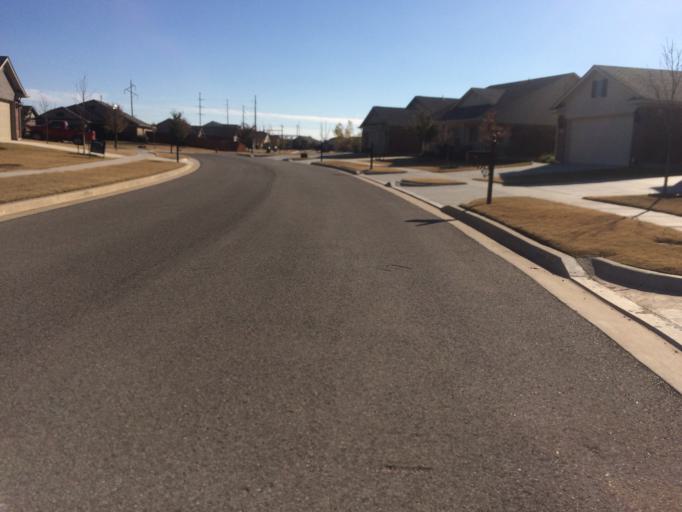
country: US
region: Oklahoma
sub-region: Cleveland County
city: Norman
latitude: 35.2501
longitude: -97.4556
